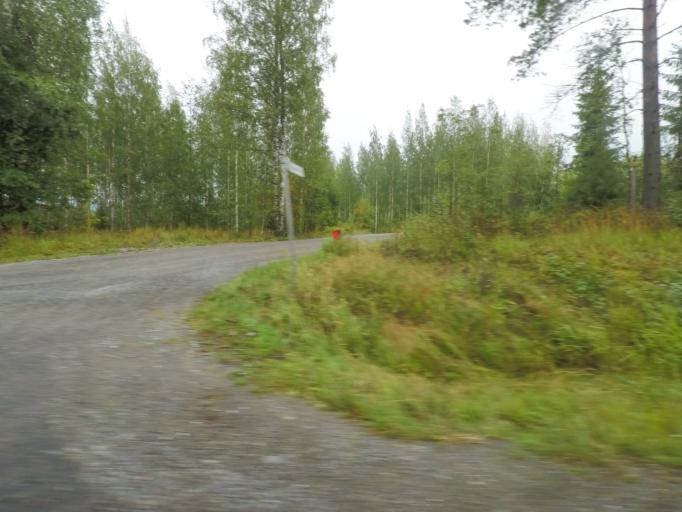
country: FI
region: Southern Savonia
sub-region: Pieksaemaeki
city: Joroinen
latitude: 62.1205
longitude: 27.8389
